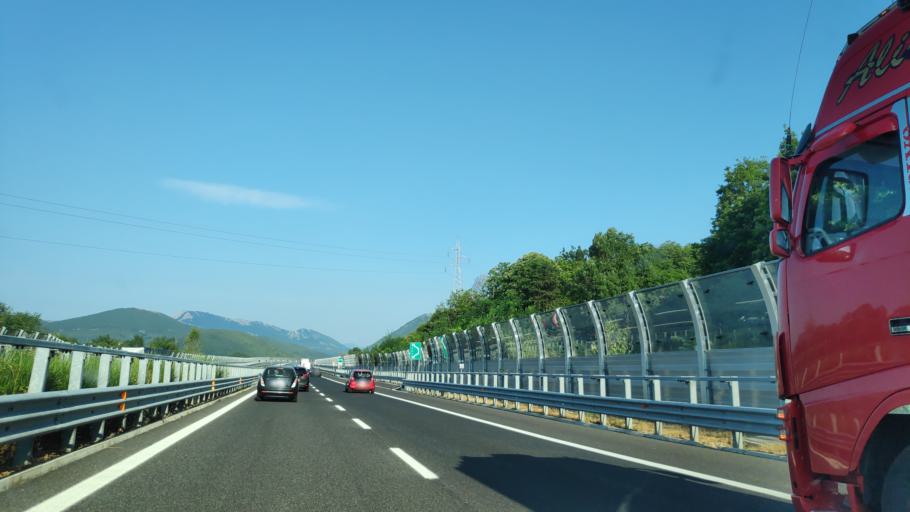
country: IT
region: Basilicate
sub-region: Provincia di Potenza
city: Lagonegro
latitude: 40.1298
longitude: 15.7683
